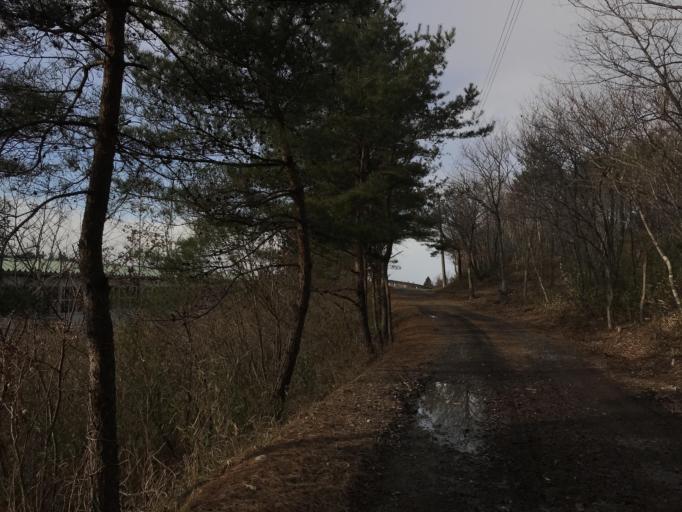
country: JP
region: Iwate
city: Ichinoseki
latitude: 38.8780
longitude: 141.1399
